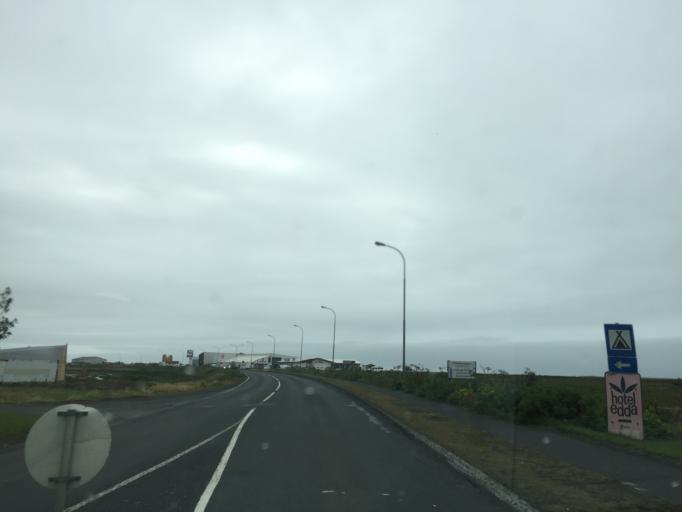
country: IS
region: South
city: Vestmannaeyjar
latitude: 63.4189
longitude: -19.0053
